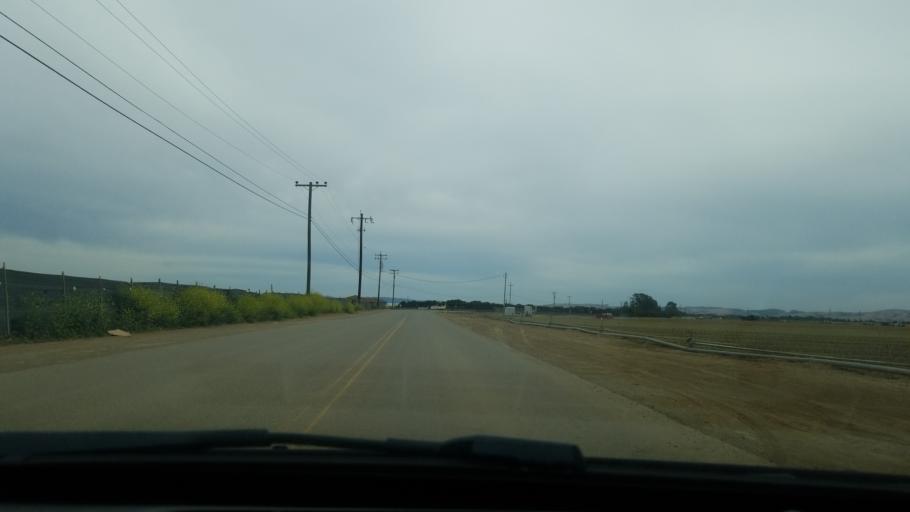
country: US
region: California
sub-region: San Luis Obispo County
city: Nipomo
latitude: 34.9971
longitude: -120.5151
